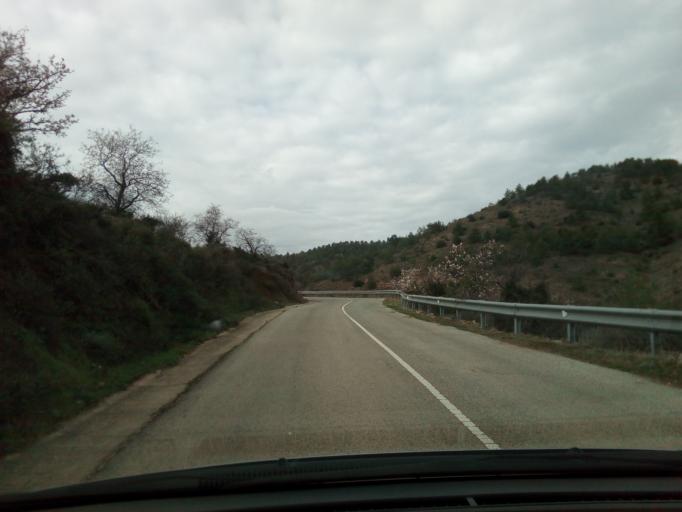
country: CY
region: Lefkosia
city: Klirou
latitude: 34.9742
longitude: 33.1793
